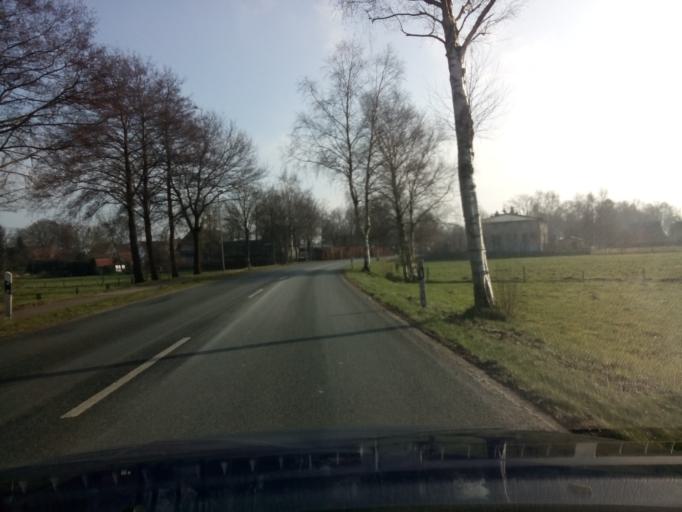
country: DE
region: Lower Saxony
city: Grasberg
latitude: 53.1573
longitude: 8.9578
